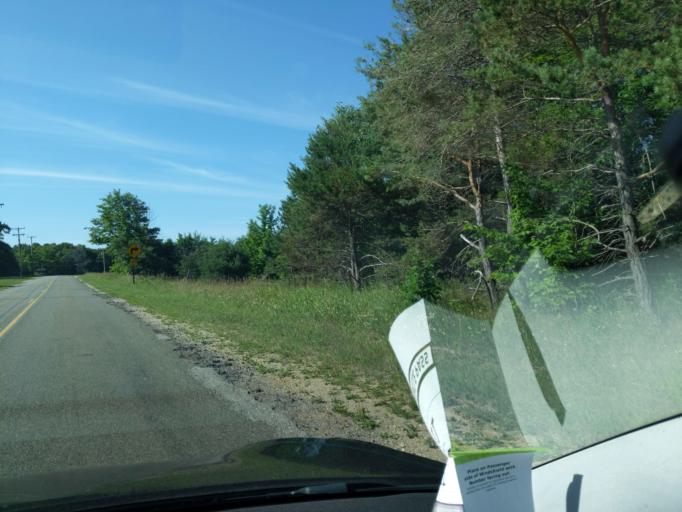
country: US
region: Michigan
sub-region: Mackinac County
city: Saint Ignace
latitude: 45.7016
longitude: -84.7316
